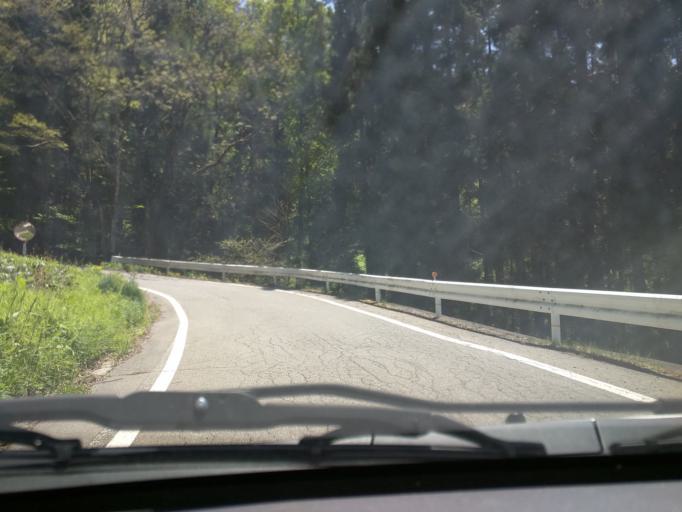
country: JP
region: Nagano
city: Nagano-shi
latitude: 36.6740
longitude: 138.1103
